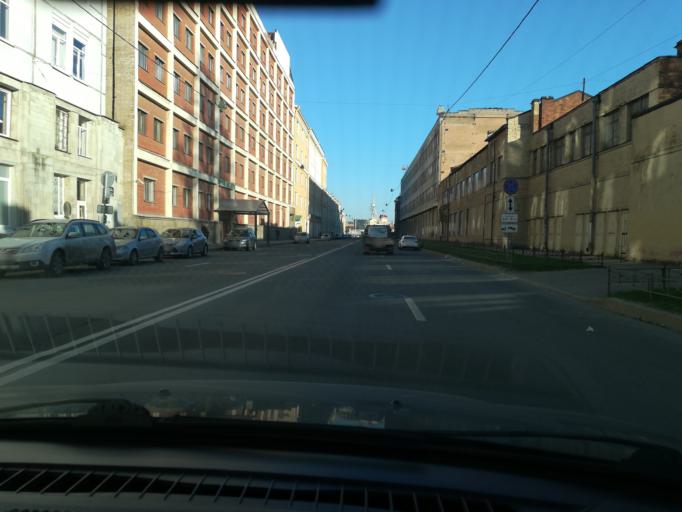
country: RU
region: St.-Petersburg
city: Vasyl'evsky Ostrov
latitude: 59.9310
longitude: 30.2651
